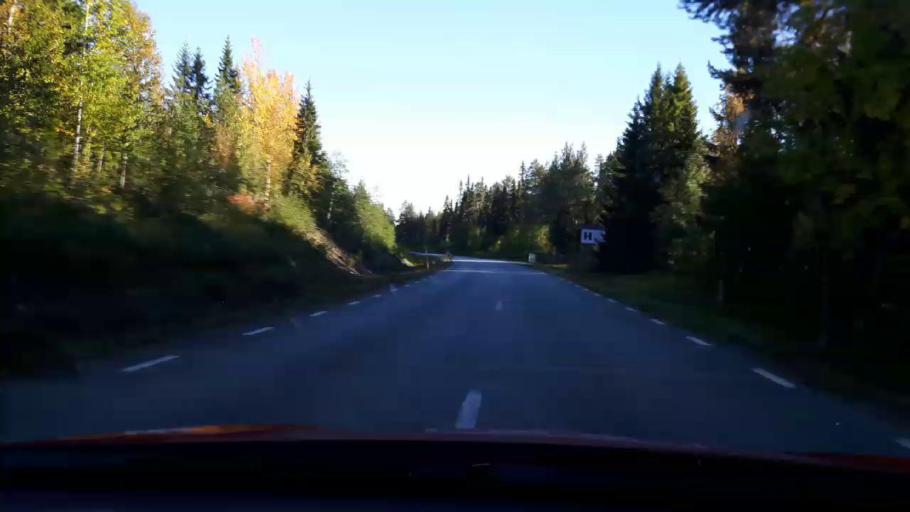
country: SE
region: Jaemtland
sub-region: OEstersunds Kommun
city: Lit
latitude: 63.7517
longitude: 14.7157
